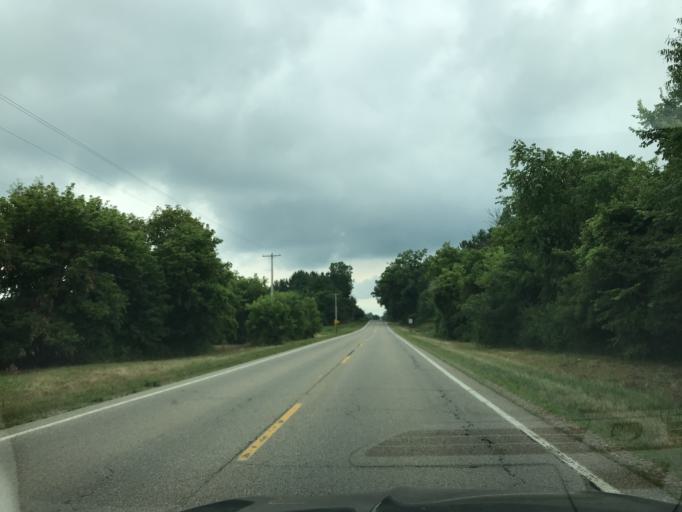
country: US
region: Michigan
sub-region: Eaton County
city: Grand Ledge
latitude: 42.8040
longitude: -84.7703
